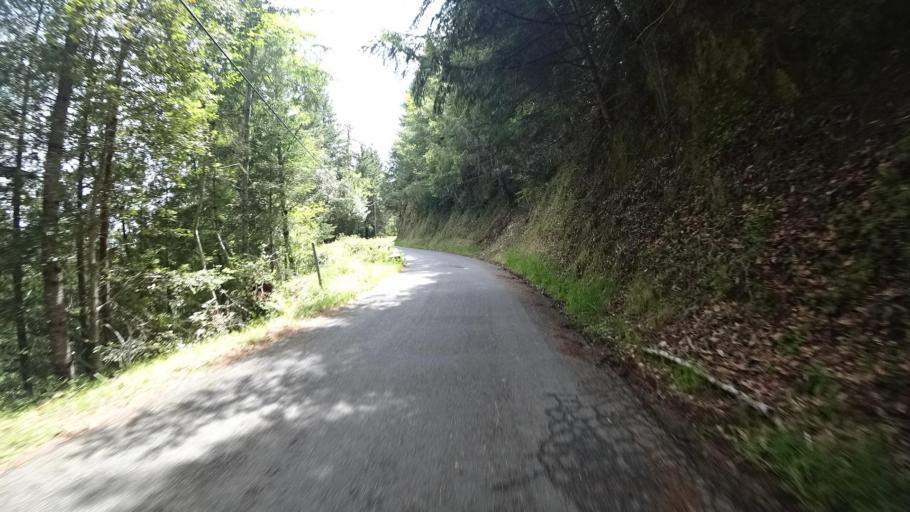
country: US
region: California
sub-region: Humboldt County
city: Blue Lake
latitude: 40.7584
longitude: -123.9133
